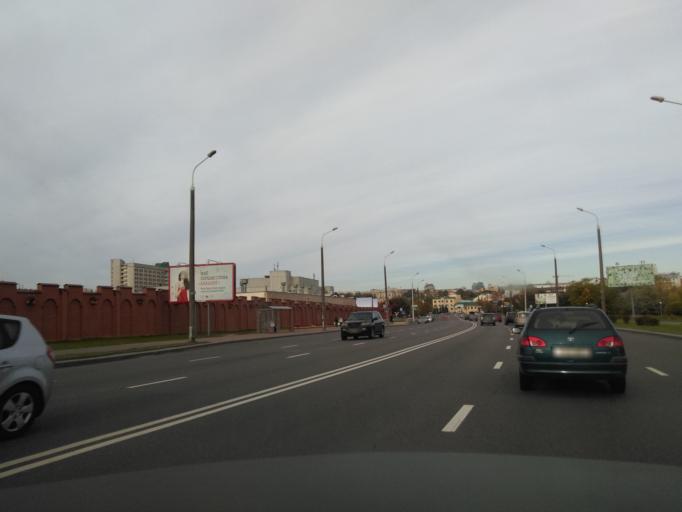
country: BY
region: Minsk
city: Minsk
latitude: 53.8934
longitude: 27.5722
